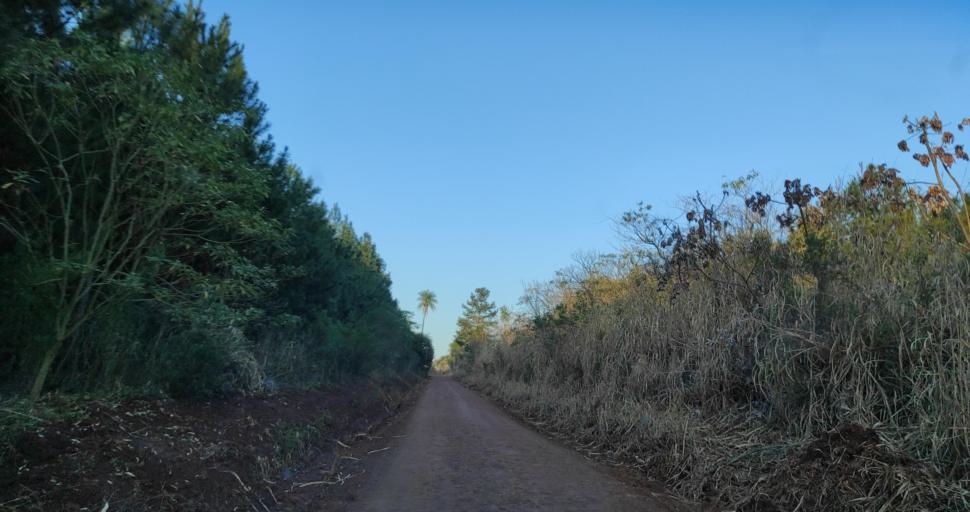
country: AR
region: Misiones
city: Capiovi
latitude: -26.8807
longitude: -55.1103
